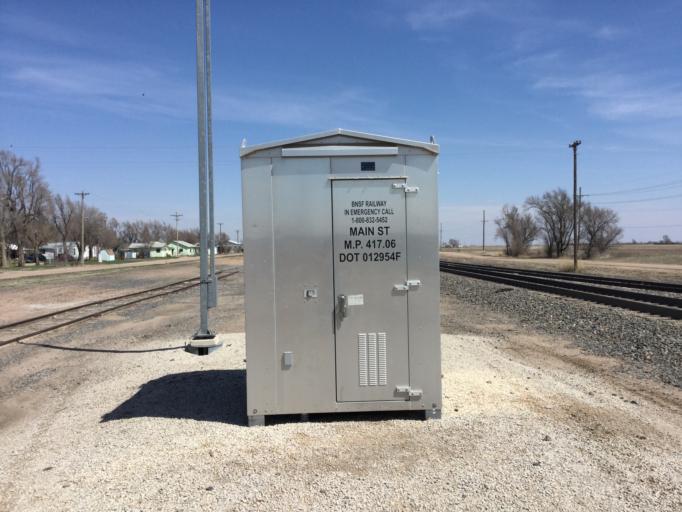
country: US
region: Kansas
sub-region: Kearny County
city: Lakin
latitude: 37.9786
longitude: -101.1326
